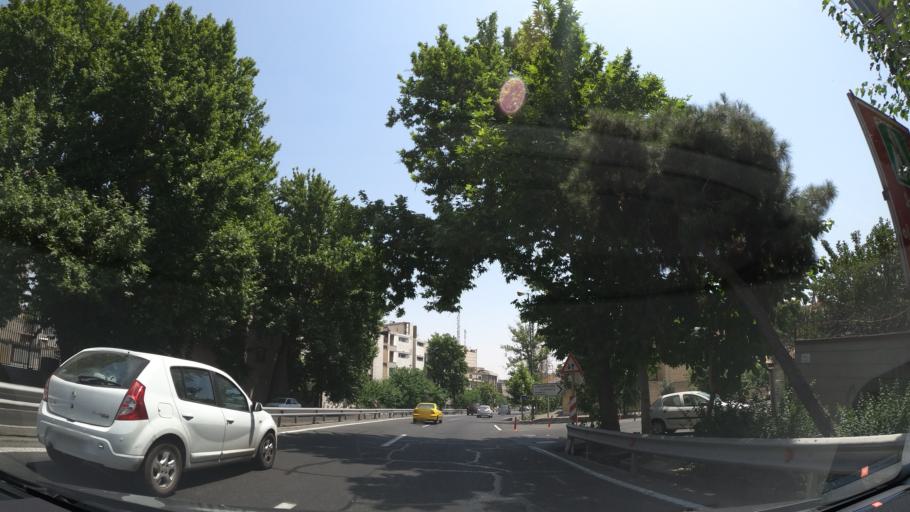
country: IR
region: Tehran
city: Tehran
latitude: 35.7211
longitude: 51.4262
